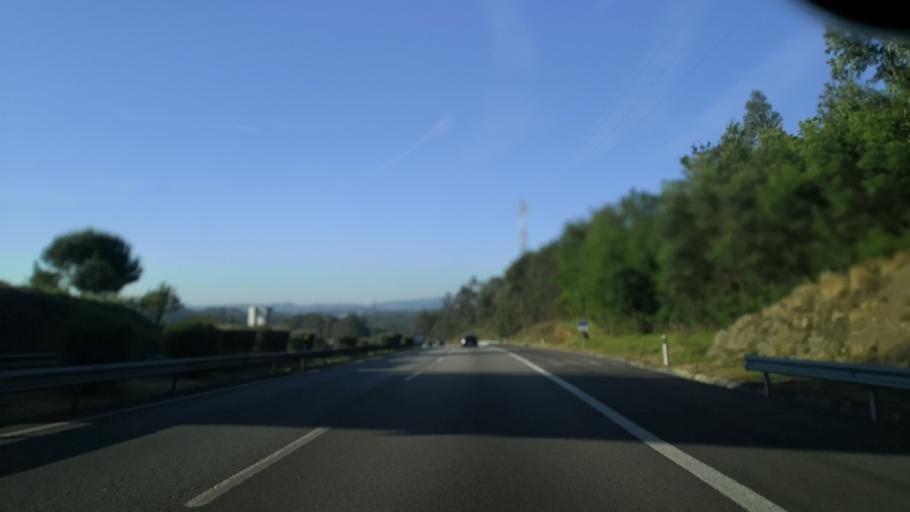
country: PT
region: Porto
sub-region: Santo Tirso
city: Santo Tirso
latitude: 41.3424
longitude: -8.5063
